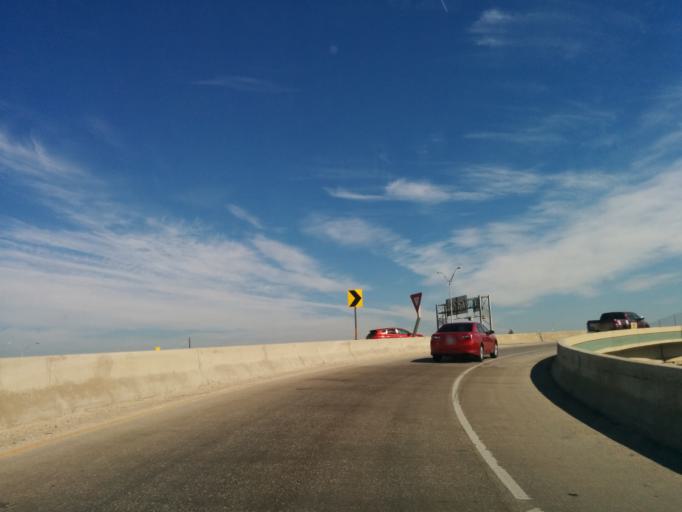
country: US
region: Texas
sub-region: Bexar County
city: Shavano Park
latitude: 29.5902
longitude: -98.5998
